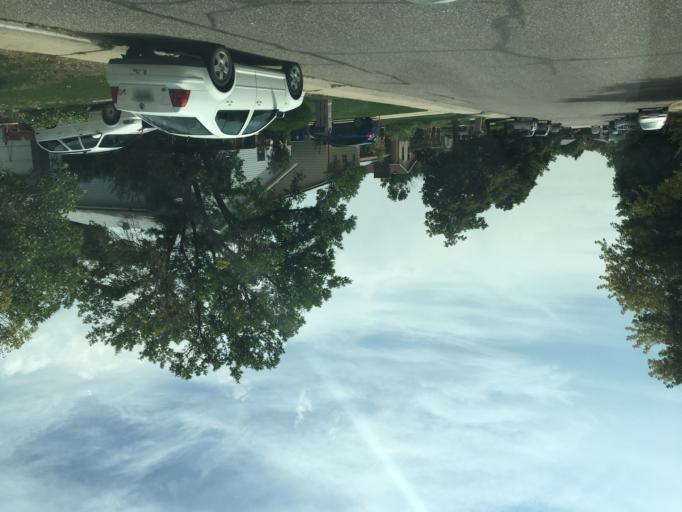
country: US
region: Colorado
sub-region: Adams County
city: Aurora
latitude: 39.7338
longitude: -104.7994
